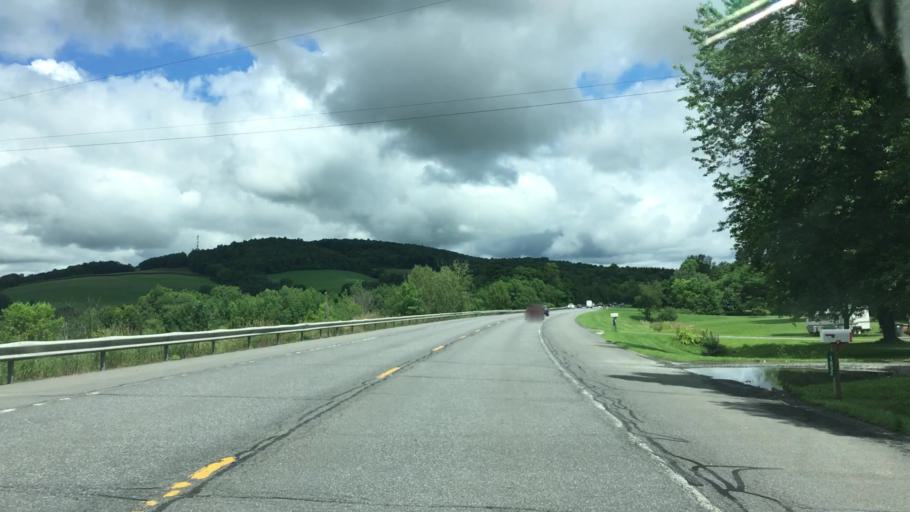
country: US
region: New York
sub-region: Rensselaer County
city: Poestenkill
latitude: 42.7975
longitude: -73.5671
